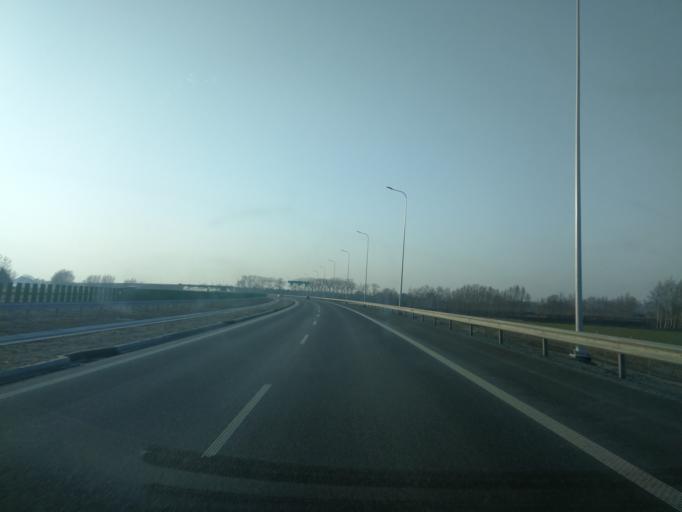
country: PL
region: Warmian-Masurian Voivodeship
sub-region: Powiat elblaski
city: Elblag
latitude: 54.1621
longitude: 19.3547
